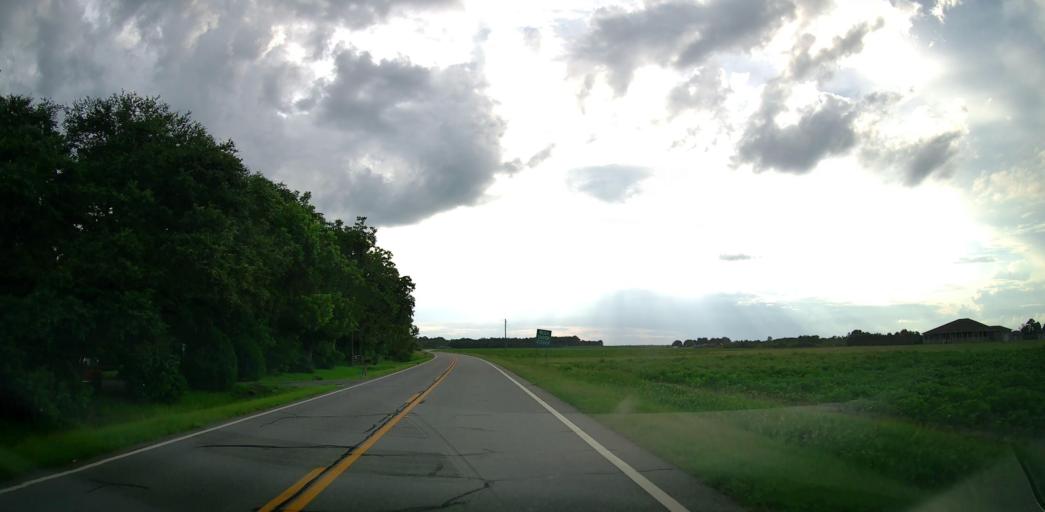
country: US
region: Georgia
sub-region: Pulaski County
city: Hawkinsville
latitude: 32.2960
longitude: -83.5347
